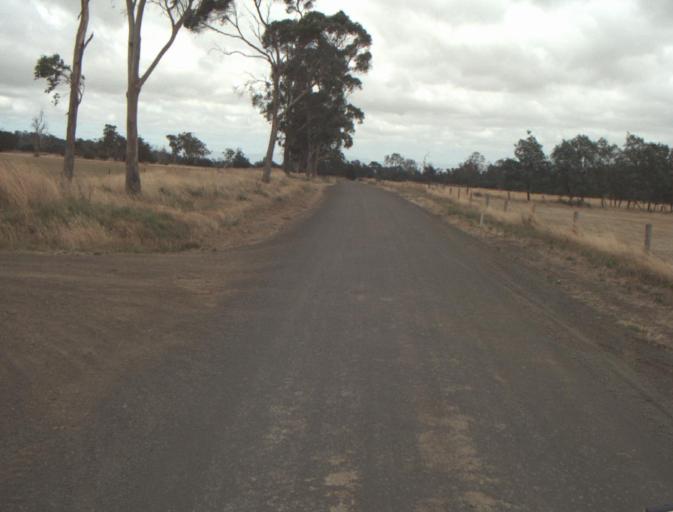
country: AU
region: Tasmania
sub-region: Northern Midlands
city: Evandale
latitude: -41.5243
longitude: 147.3645
